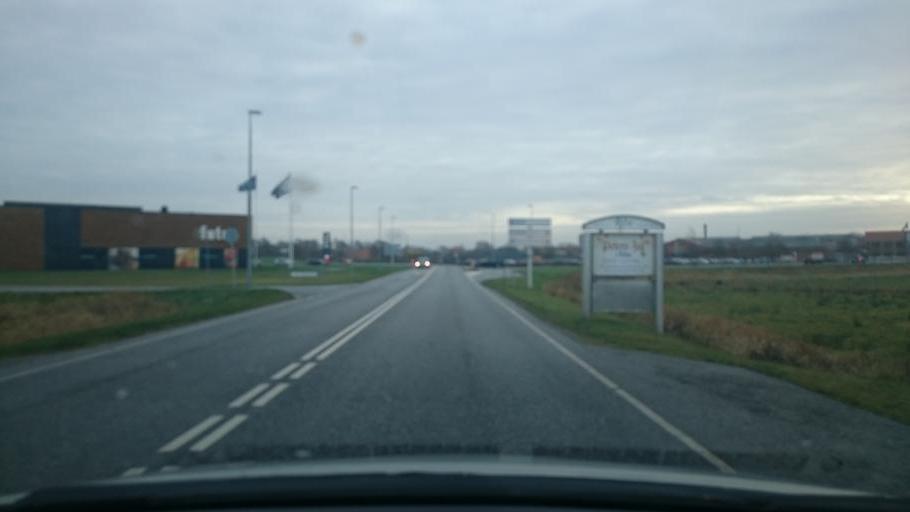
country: DK
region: South Denmark
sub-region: Esbjerg Kommune
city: Ribe
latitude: 55.3343
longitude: 8.7683
